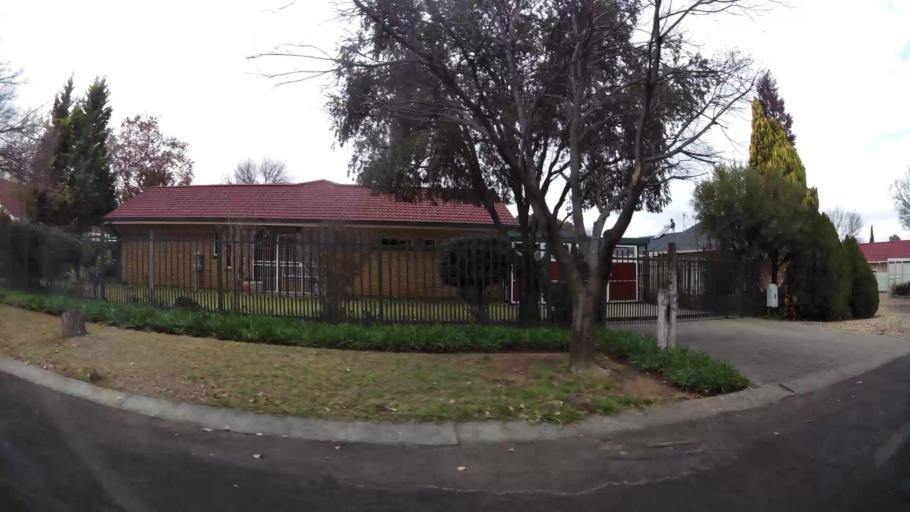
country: ZA
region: Orange Free State
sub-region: Fezile Dabi District Municipality
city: Kroonstad
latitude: -27.6331
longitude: 27.2412
